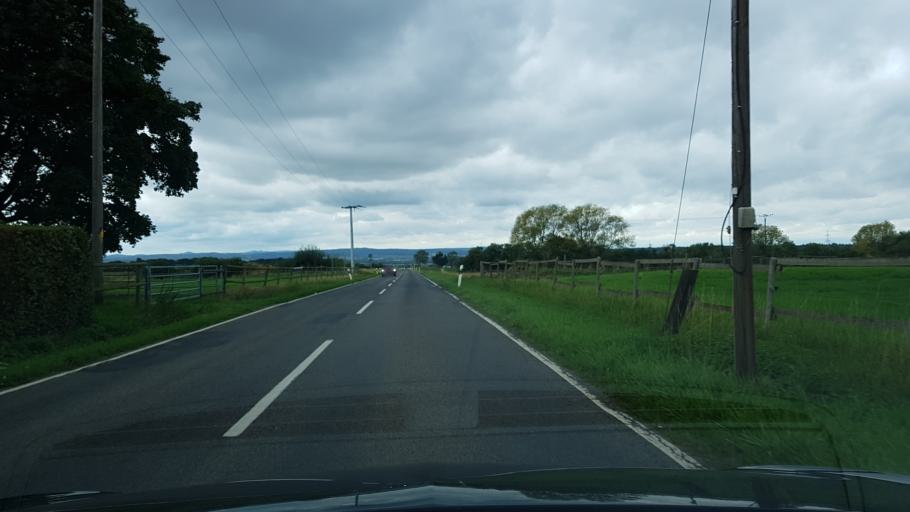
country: DE
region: North Rhine-Westphalia
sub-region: Regierungsbezirk Koln
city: Wachtberg
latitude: 50.6192
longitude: 7.1159
